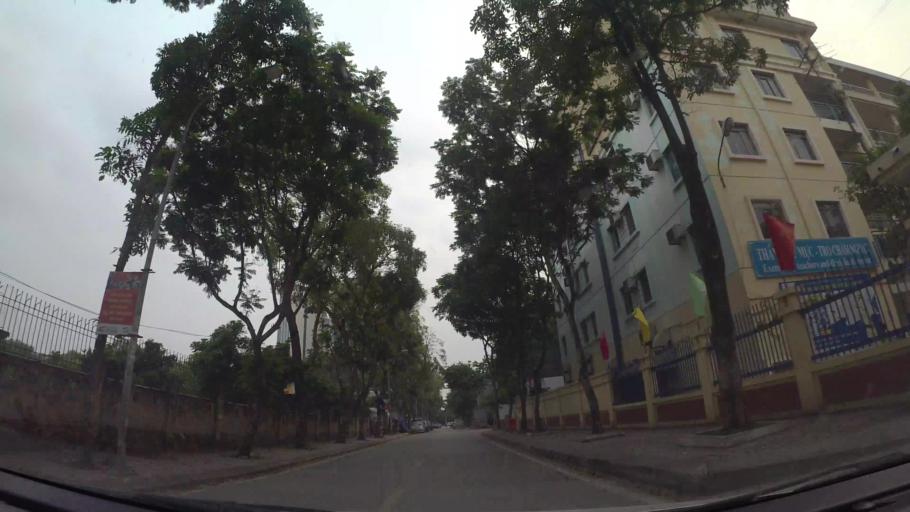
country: VN
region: Ha Noi
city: Cau Dien
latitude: 21.0302
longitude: 105.7675
